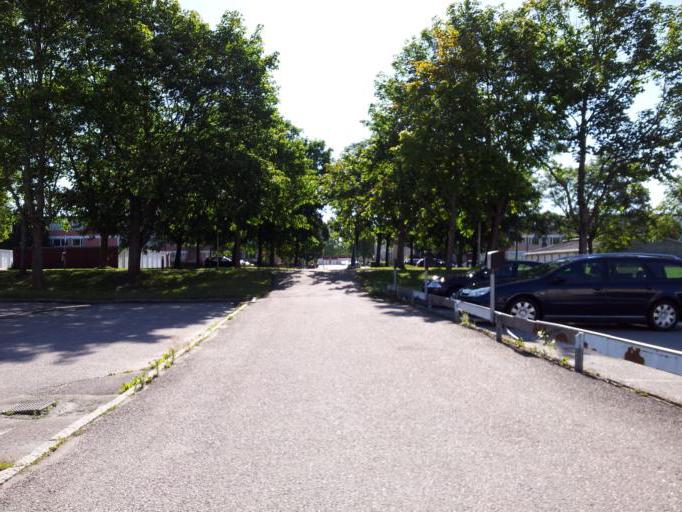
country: SE
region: Uppsala
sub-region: Uppsala Kommun
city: Uppsala
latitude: 59.8768
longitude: 17.6546
